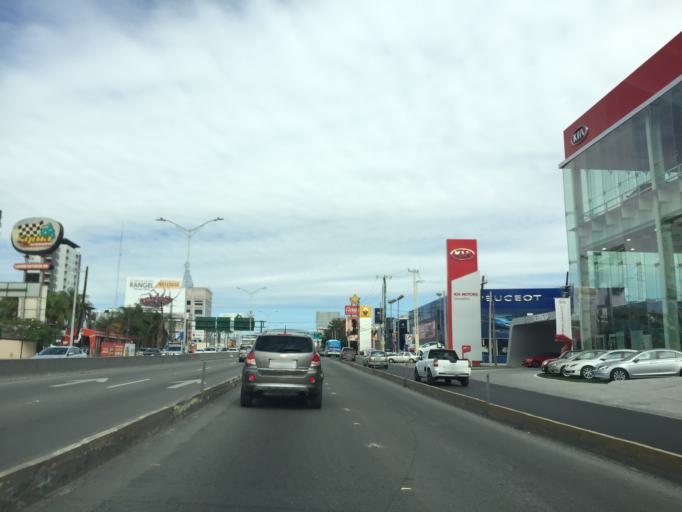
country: MX
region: Nuevo Leon
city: Garza Garcia
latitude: 25.6744
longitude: -100.3524
